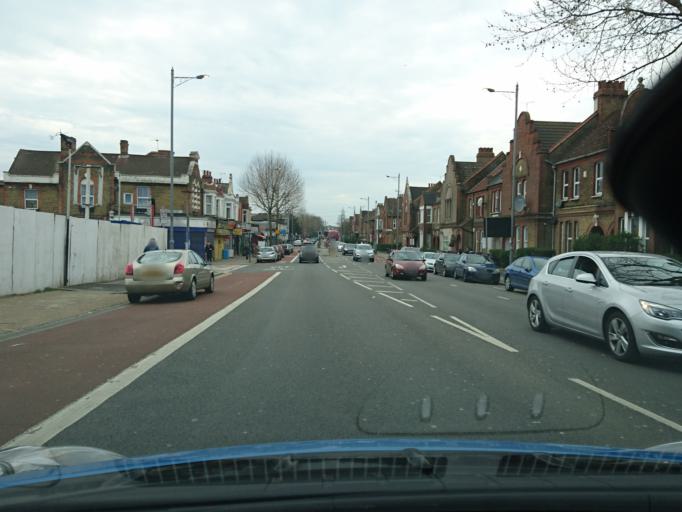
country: GB
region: England
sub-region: Greater London
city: Walthamstow
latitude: 51.5699
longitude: -0.0261
